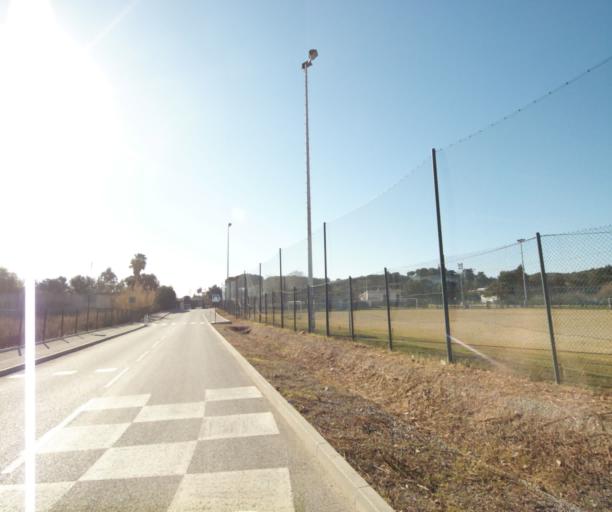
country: FR
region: Provence-Alpes-Cote d'Azur
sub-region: Departement des Alpes-Maritimes
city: Biot
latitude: 43.6050
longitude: 7.0804
